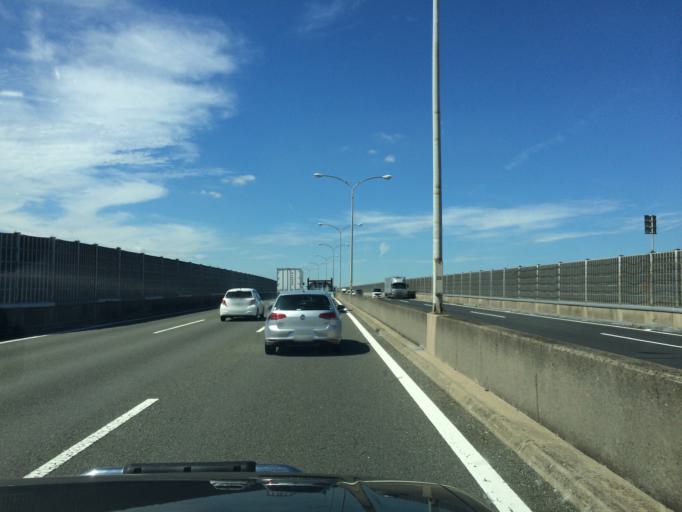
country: JP
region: Osaka
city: Matsubara
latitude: 34.5328
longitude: 135.5250
